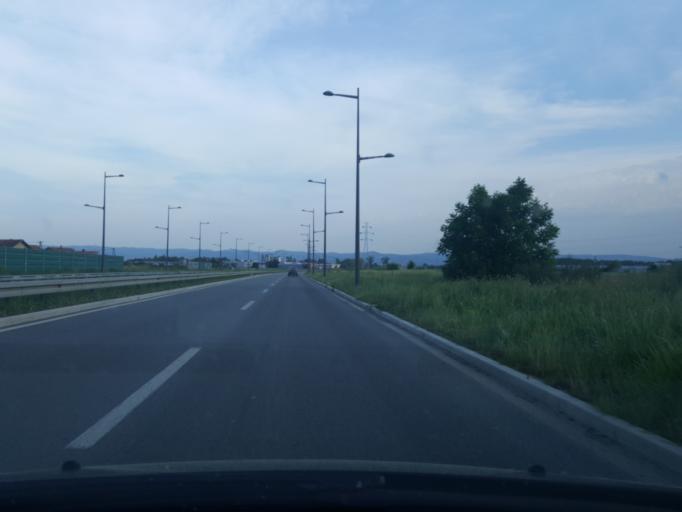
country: RS
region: Autonomna Pokrajina Vojvodina
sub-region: Juznobacki Okrug
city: Novi Sad
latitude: 45.2964
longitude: 19.8077
